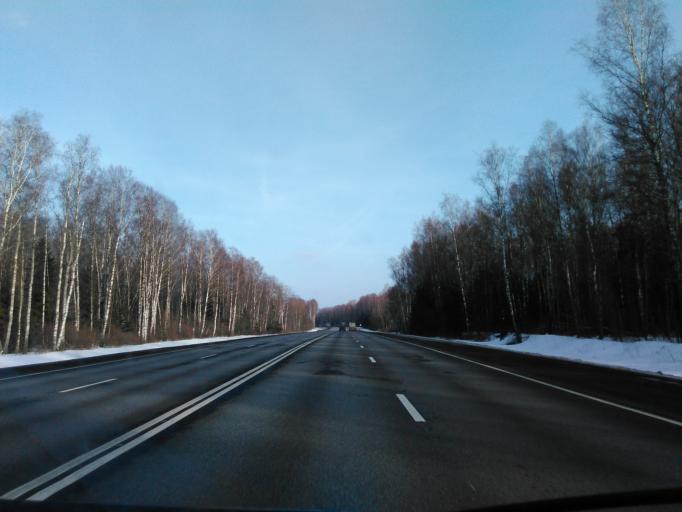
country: RU
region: Smolensk
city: Vyaz'ma
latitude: 55.1878
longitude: 34.0499
